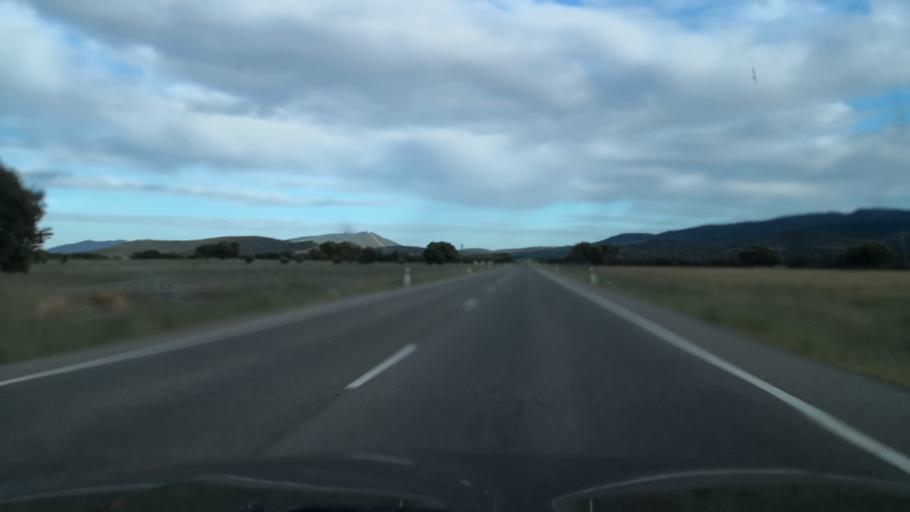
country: ES
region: Extremadura
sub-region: Provincia de Caceres
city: Torrejoncillo
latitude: 39.8682
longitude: -6.4379
